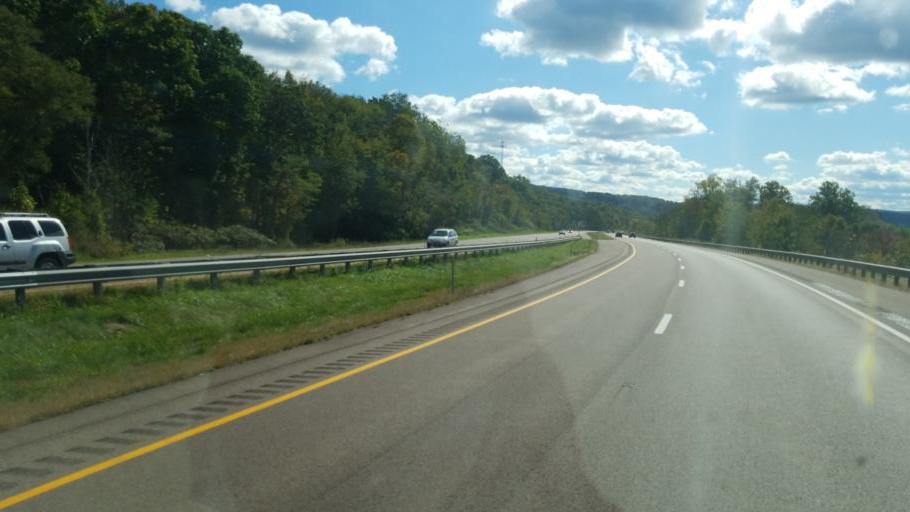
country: US
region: Maryland
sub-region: Garrett County
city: Oakland
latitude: 39.6757
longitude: -79.3824
